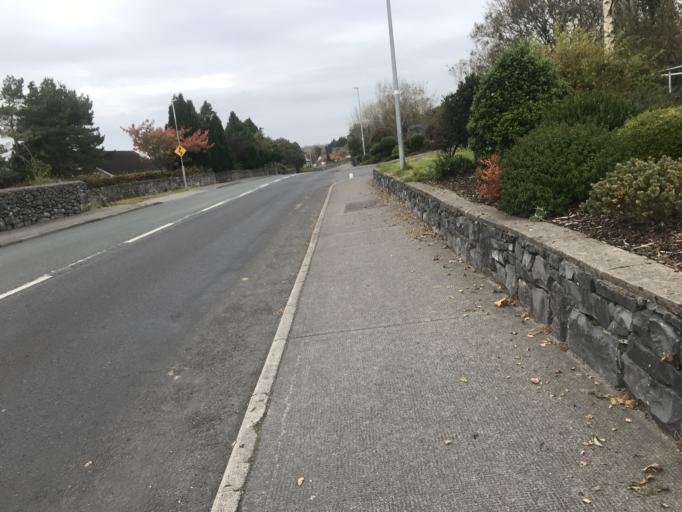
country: IE
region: Connaught
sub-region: County Galway
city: Gaillimh
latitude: 53.2942
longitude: -9.0529
